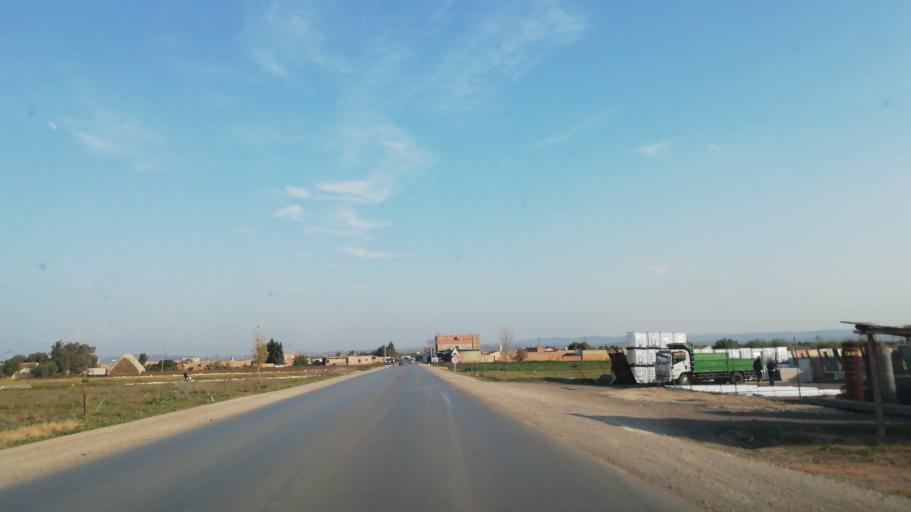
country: DZ
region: Relizane
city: Djidiouia
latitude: 35.8973
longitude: 0.6894
